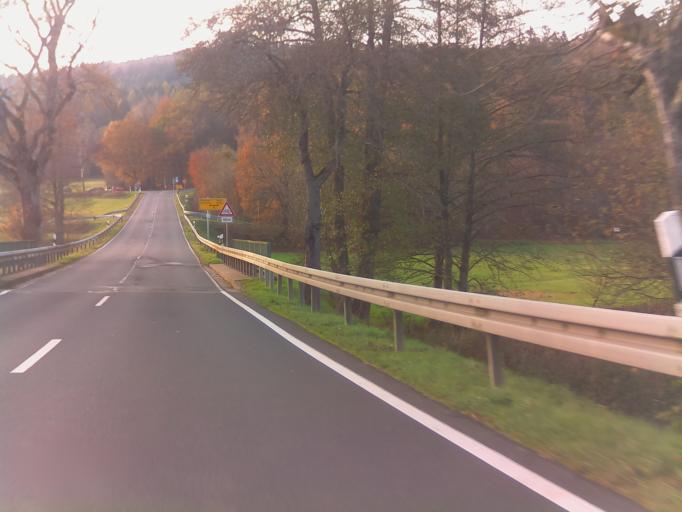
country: DE
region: Bavaria
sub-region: Regierungsbezirk Unterfranken
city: Zeitlofs
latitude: 50.2634
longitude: 9.6488
